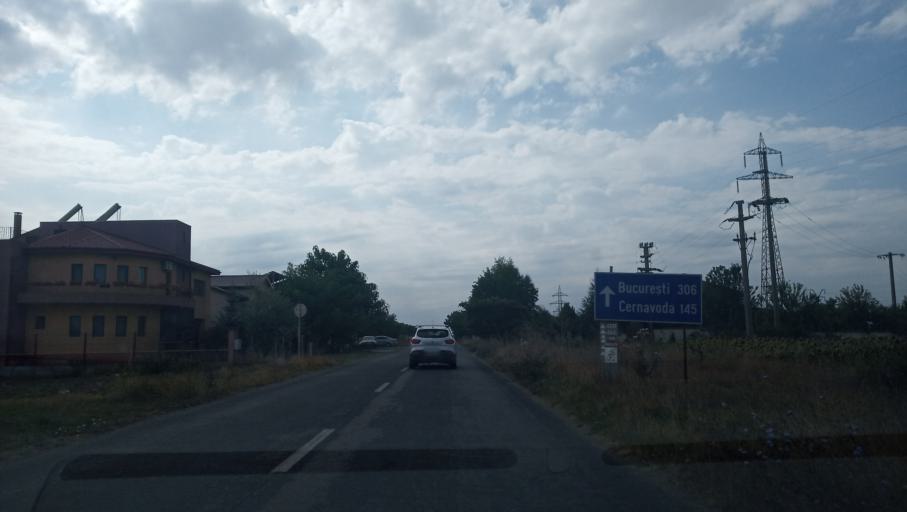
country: RO
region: Constanta
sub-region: Municipiul Mangalia
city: Mangalia
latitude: 43.8158
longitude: 28.5617
